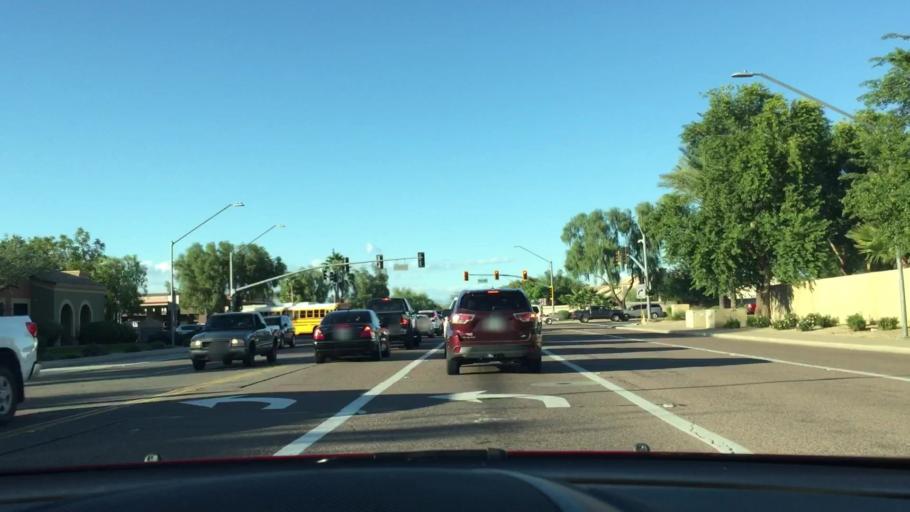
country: US
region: Arizona
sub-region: Maricopa County
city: Sun City
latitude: 33.6809
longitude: -112.2203
